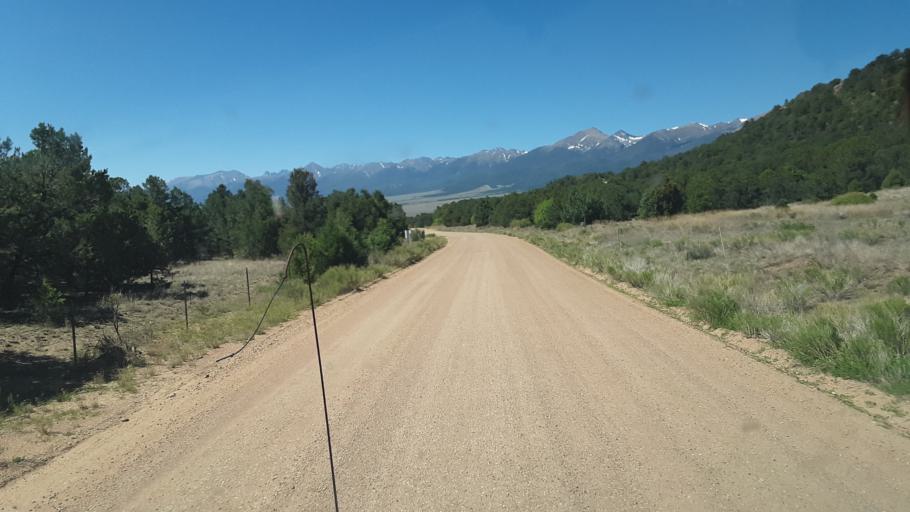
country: US
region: Colorado
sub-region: Custer County
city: Westcliffe
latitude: 38.2607
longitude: -105.5487
